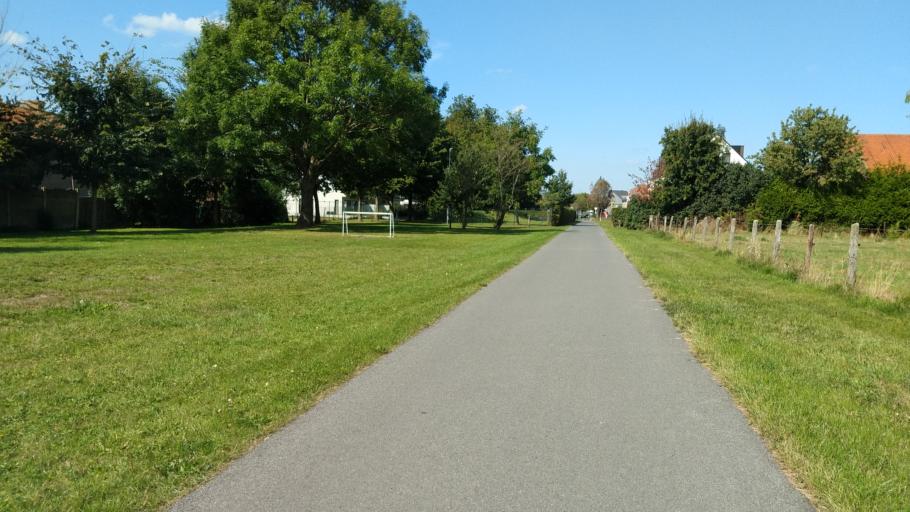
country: BE
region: Flanders
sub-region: Provincie Oost-Vlaanderen
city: Assenede
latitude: 51.2234
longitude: 3.7550
